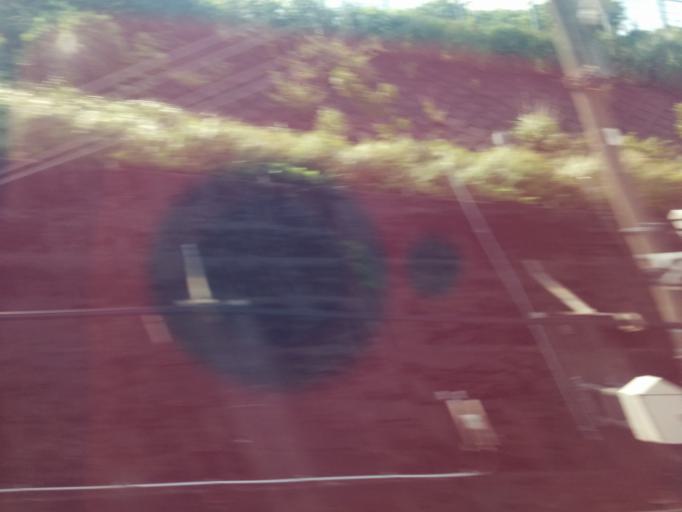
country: JP
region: Shizuoka
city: Shimada
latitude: 34.7943
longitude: 138.1739
